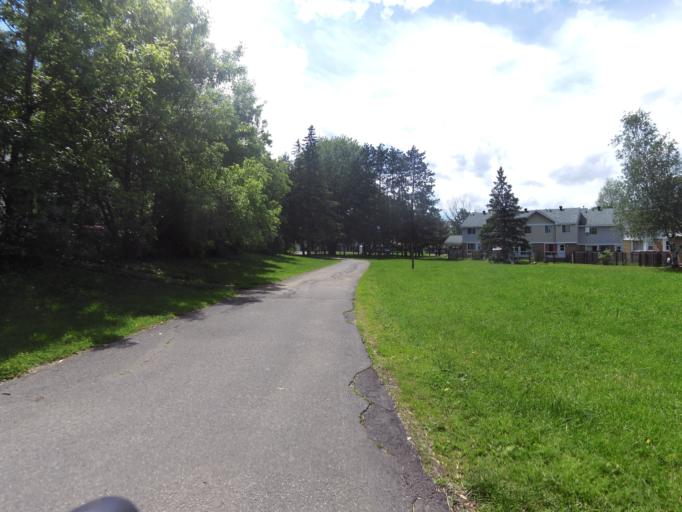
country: CA
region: Ontario
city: Ottawa
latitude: 45.3576
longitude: -75.6434
